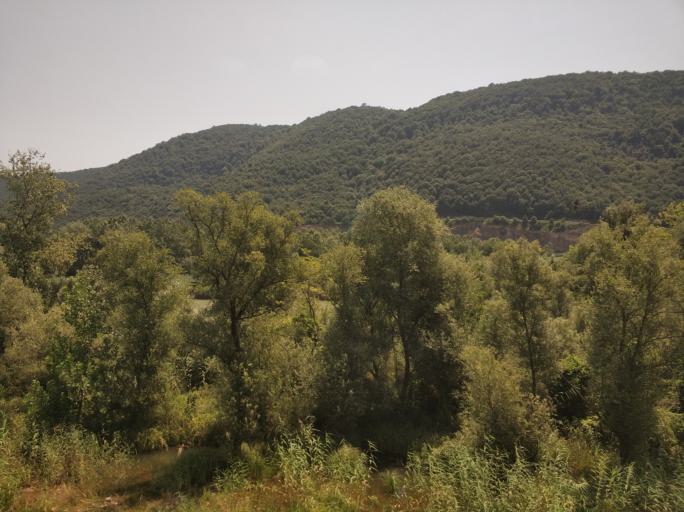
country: IR
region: Gilan
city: Pa'in-e Bazar-e Rudbar
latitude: 36.9850
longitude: 49.5583
